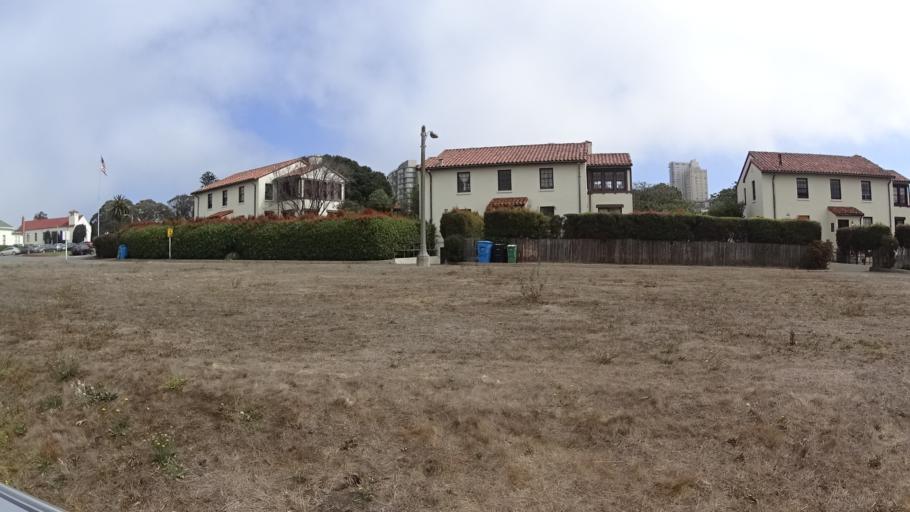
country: US
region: California
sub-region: San Francisco County
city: San Francisco
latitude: 37.8046
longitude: -122.4286
